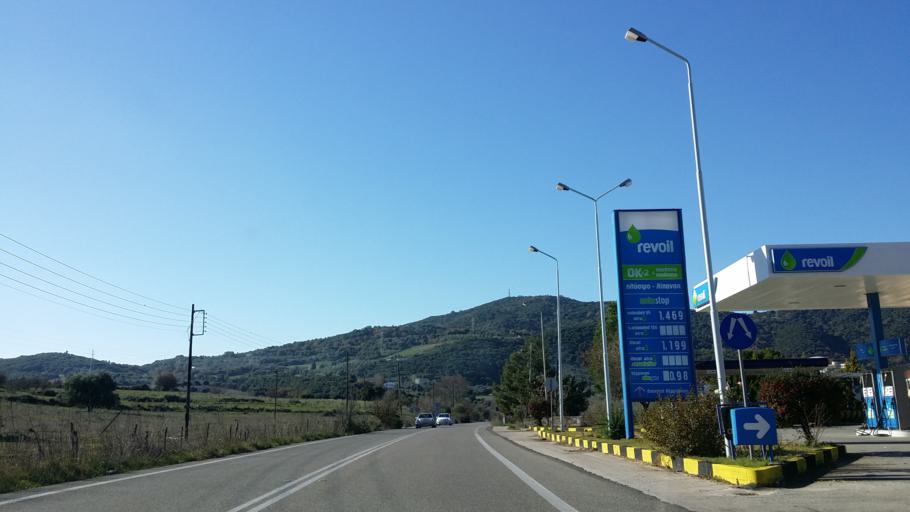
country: GR
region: West Greece
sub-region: Nomos Aitolias kai Akarnanias
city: Monastirakion
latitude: 38.9110
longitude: 20.9615
